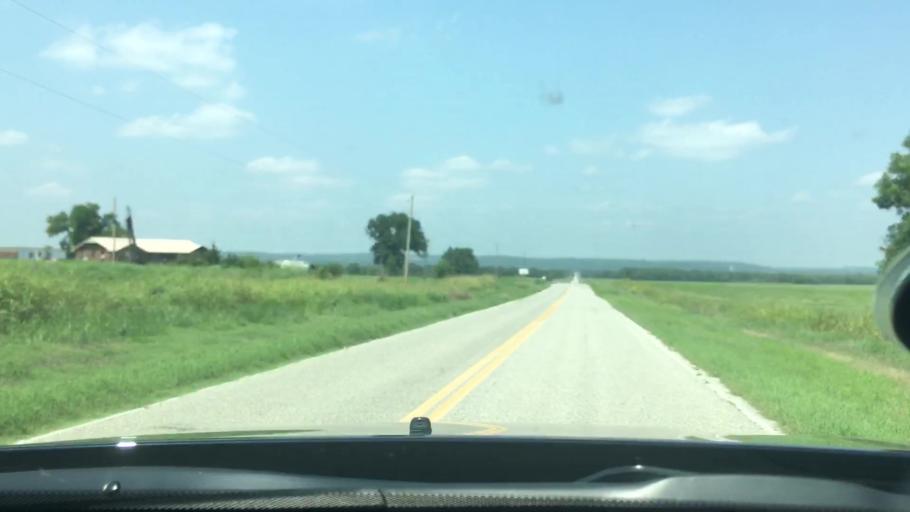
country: US
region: Oklahoma
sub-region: Johnston County
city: Tishomingo
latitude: 34.3739
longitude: -96.4961
